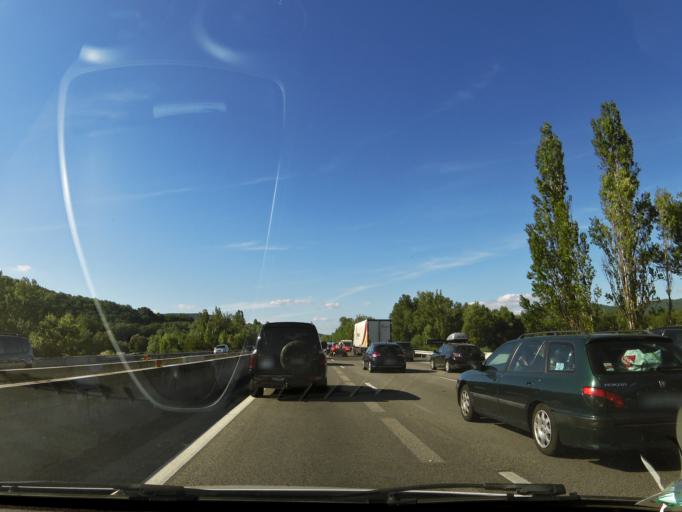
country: FR
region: Rhone-Alpes
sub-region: Departement de la Drome
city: Saint-Marcel-les-Sauzet
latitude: 44.5830
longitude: 4.8040
